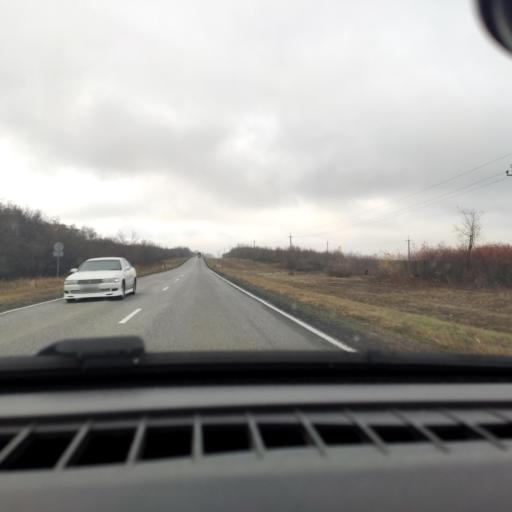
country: RU
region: Voronezj
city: Uryv-Pokrovka
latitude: 51.0931
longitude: 39.0094
